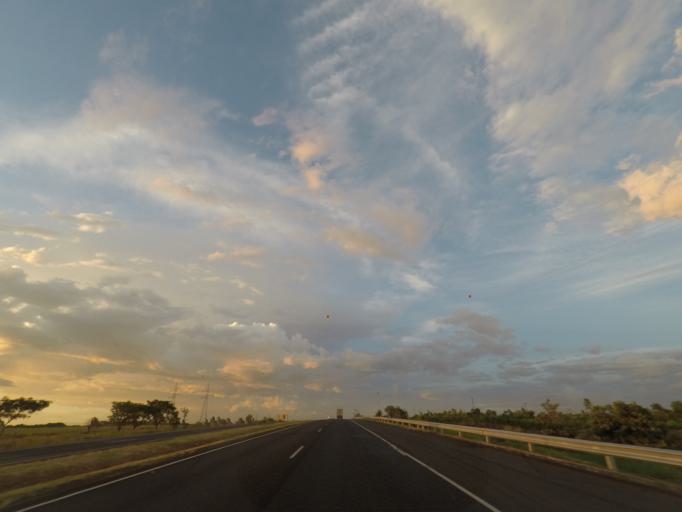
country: BR
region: Minas Gerais
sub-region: Uberaba
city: Uberaba
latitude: -19.6518
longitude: -48.0056
